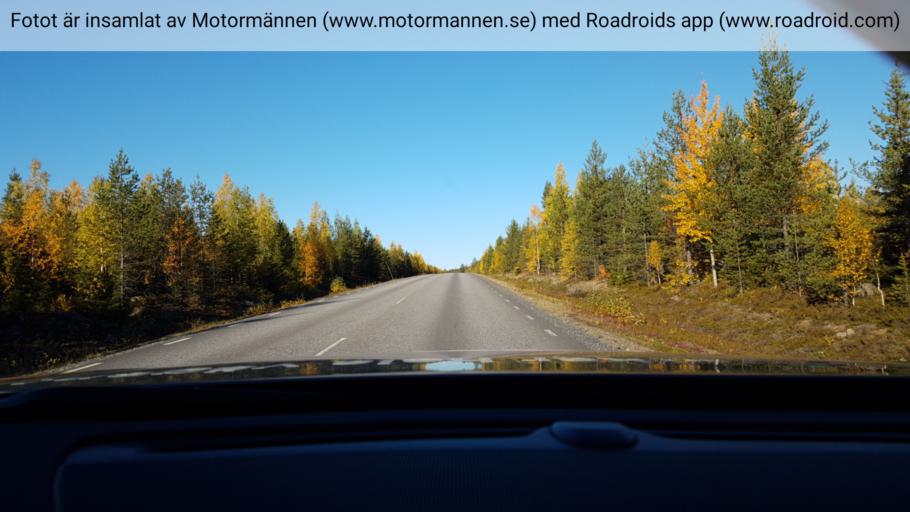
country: SE
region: Vaesterbotten
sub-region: Skelleftea Kommun
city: Storvik
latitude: 65.3265
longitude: 20.6836
